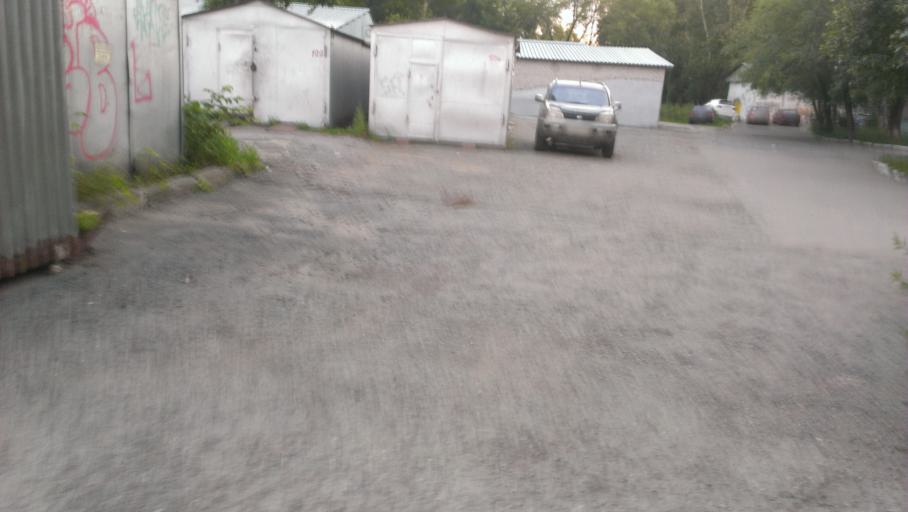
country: RU
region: Altai Krai
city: Novosilikatnyy
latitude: 53.3772
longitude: 83.6780
